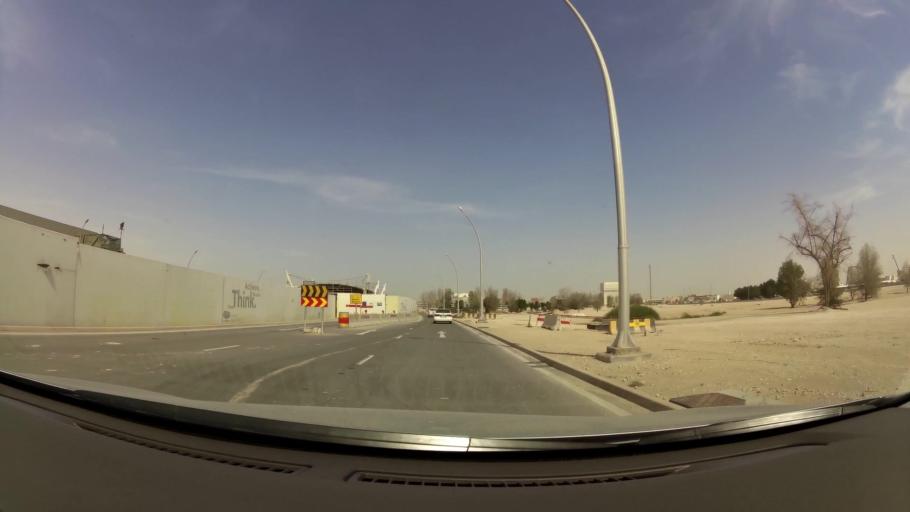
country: QA
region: Baladiyat ar Rayyan
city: Ar Rayyan
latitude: 25.3205
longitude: 51.4250
